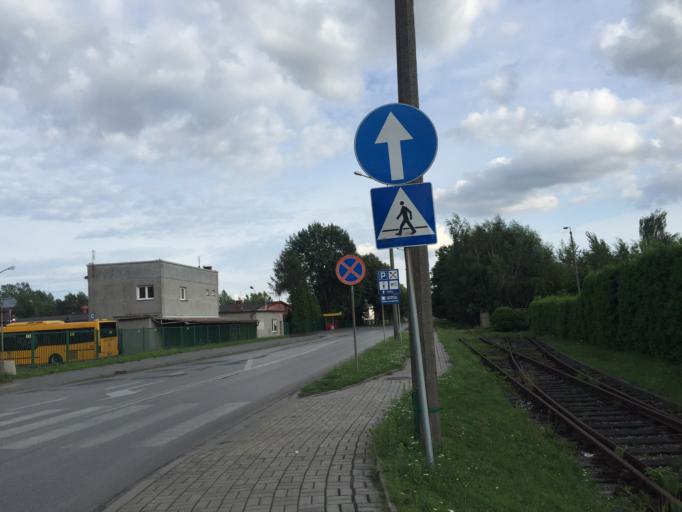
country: PL
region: Lesser Poland Voivodeship
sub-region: Powiat oswiecimski
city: Brzezinka
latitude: 50.0356
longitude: 19.1955
